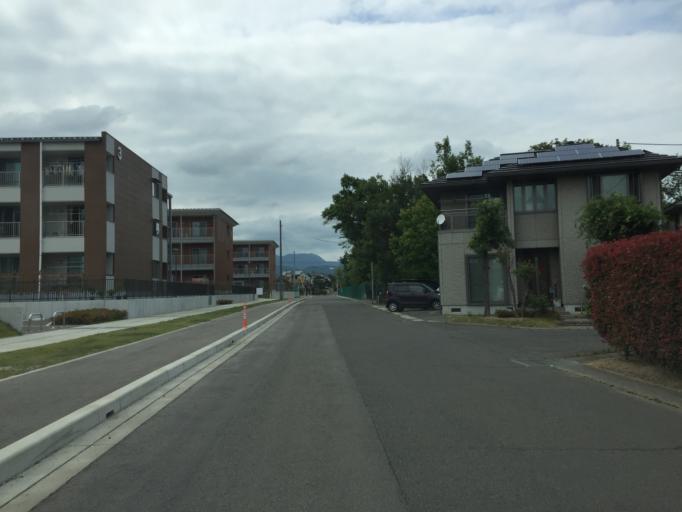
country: JP
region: Fukushima
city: Fukushima-shi
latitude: 37.7843
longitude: 140.4313
